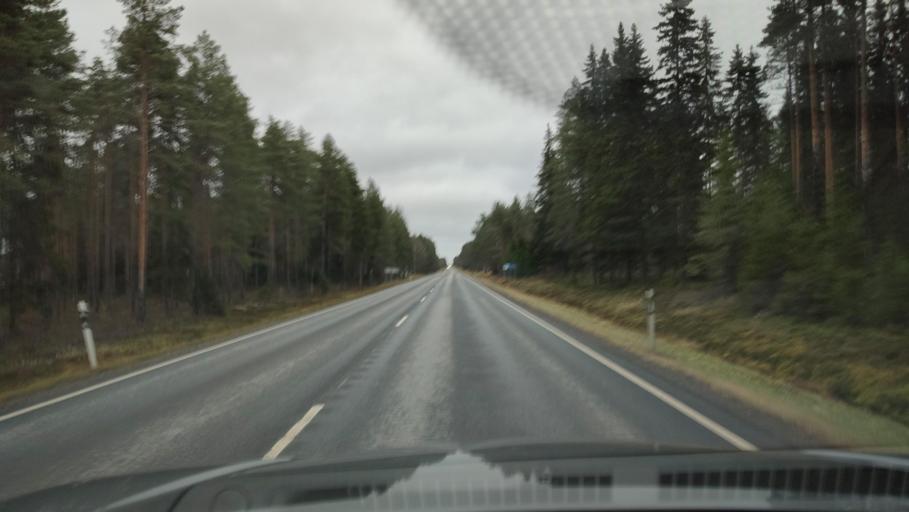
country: FI
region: Southern Ostrobothnia
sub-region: Seinaejoki
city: Kurikka
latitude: 62.5189
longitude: 22.3164
